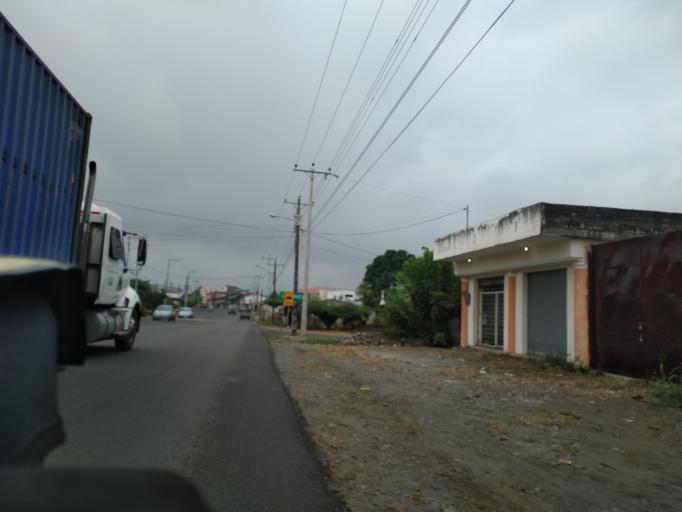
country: EC
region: Cotopaxi
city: La Mana
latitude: -0.9453
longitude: -79.3323
